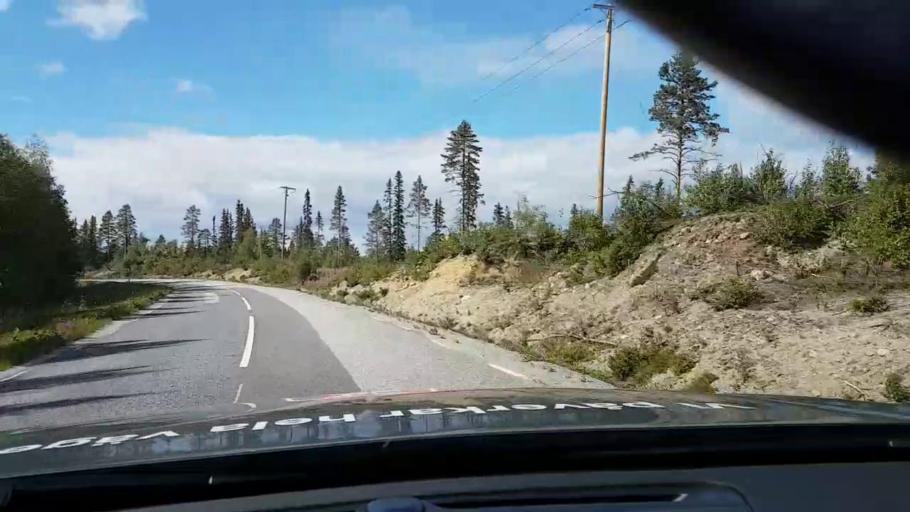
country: SE
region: Vaesterbotten
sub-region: Asele Kommun
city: Asele
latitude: 63.8277
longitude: 17.4720
